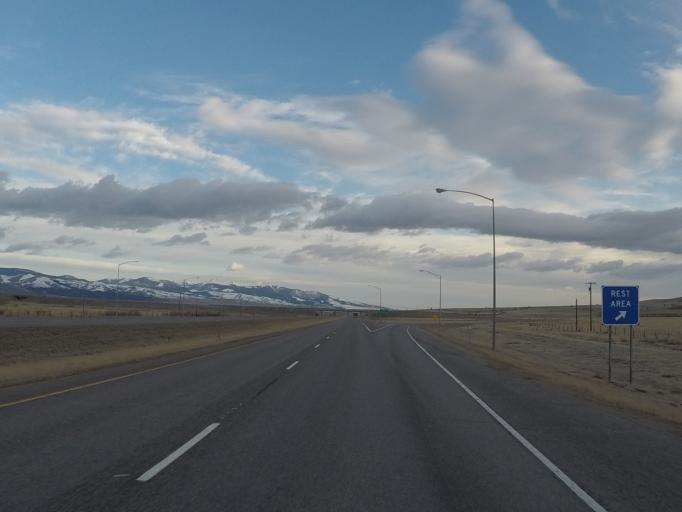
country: US
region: Montana
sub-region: Deer Lodge County
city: Warm Springs
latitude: 46.0892
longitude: -112.7904
